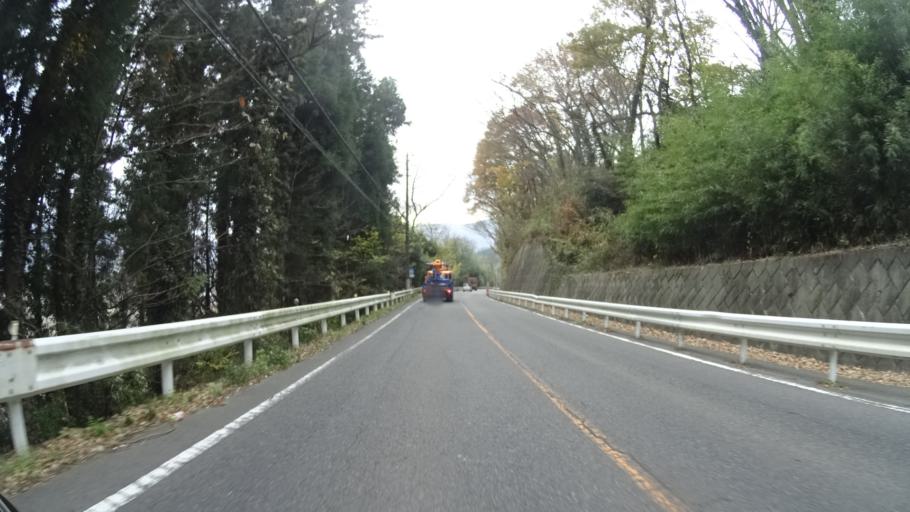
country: JP
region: Gunma
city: Numata
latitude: 36.6296
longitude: 139.0464
